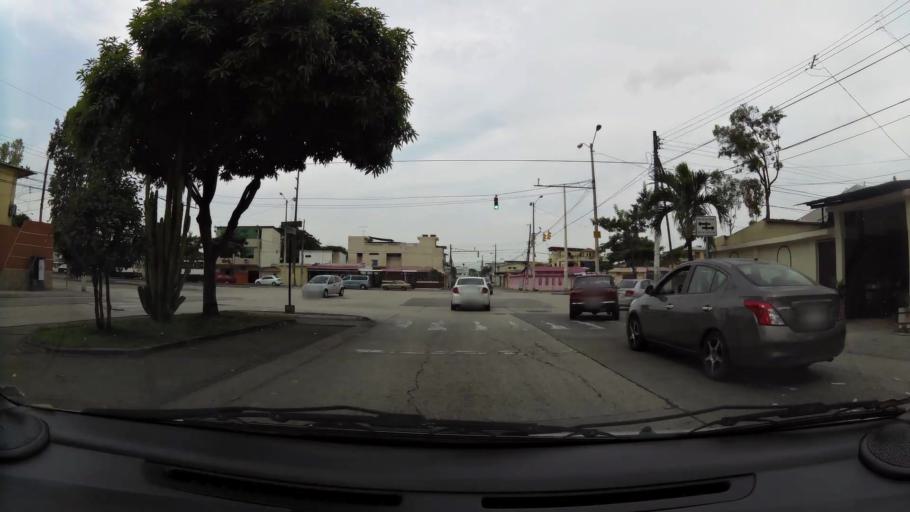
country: EC
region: Guayas
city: Eloy Alfaro
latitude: -2.1144
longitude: -79.8923
